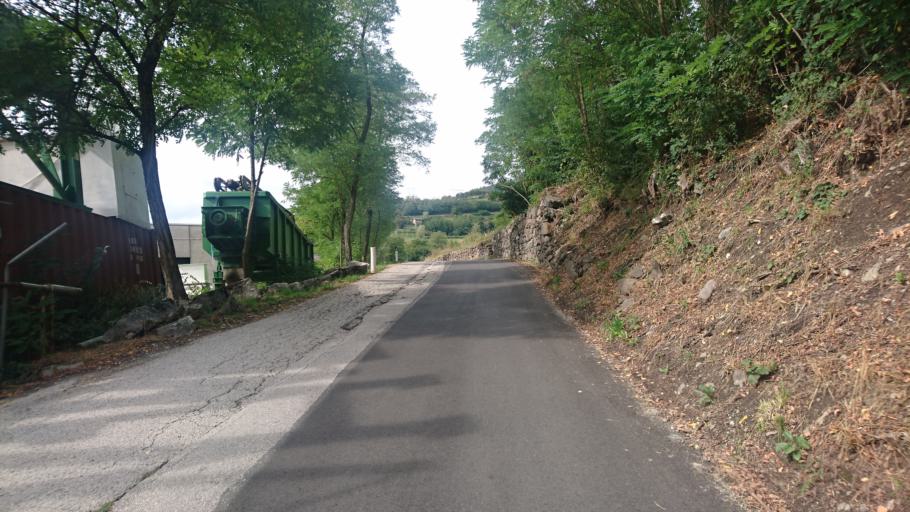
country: IT
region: Trentino-Alto Adige
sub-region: Provincia di Trento
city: Madrano-Canzolino
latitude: 46.0821
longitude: 11.2019
